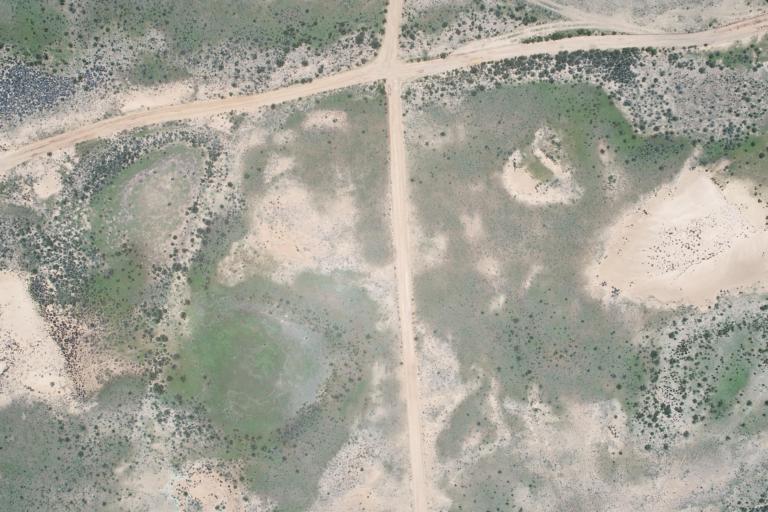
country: BO
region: La Paz
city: Patacamaya
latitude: -17.2837
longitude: -68.5059
